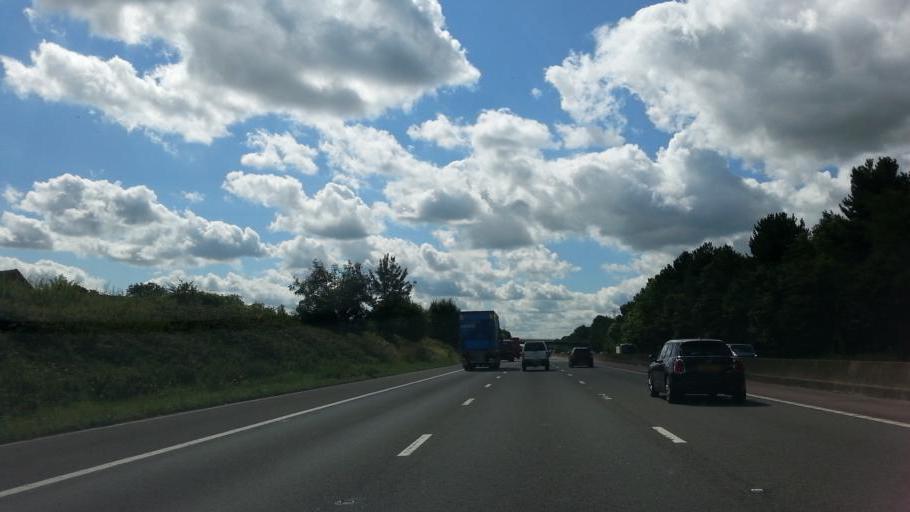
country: GB
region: England
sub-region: Leicestershire
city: Lutterworth
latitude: 52.4807
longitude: -1.1921
